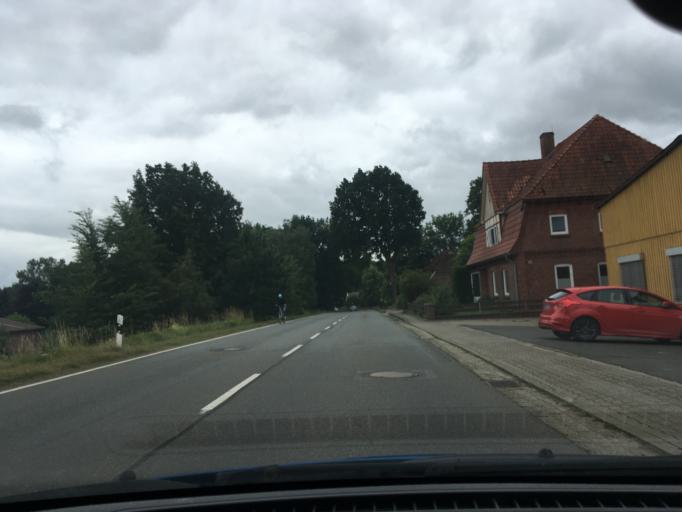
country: DE
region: Lower Saxony
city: Toppenstedt
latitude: 53.2670
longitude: 10.1190
